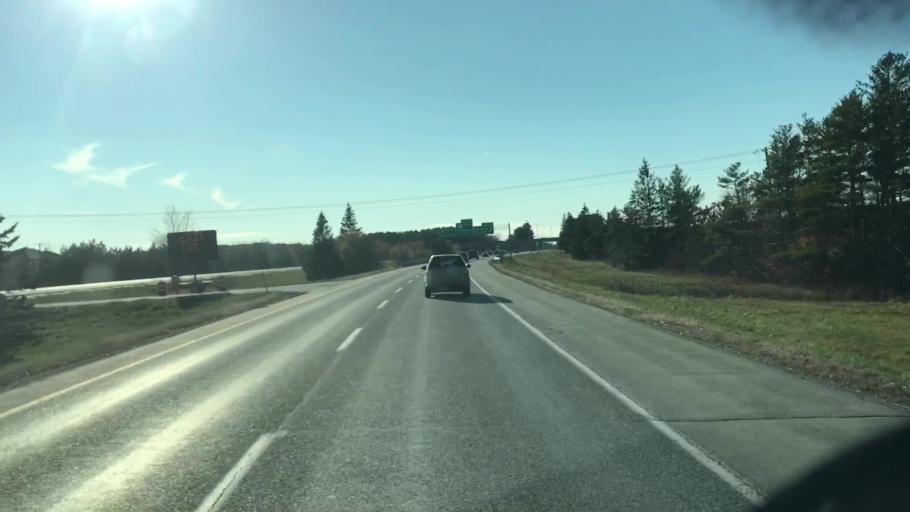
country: US
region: Maine
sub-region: Penobscot County
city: Brewer
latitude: 44.8283
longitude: -68.7474
